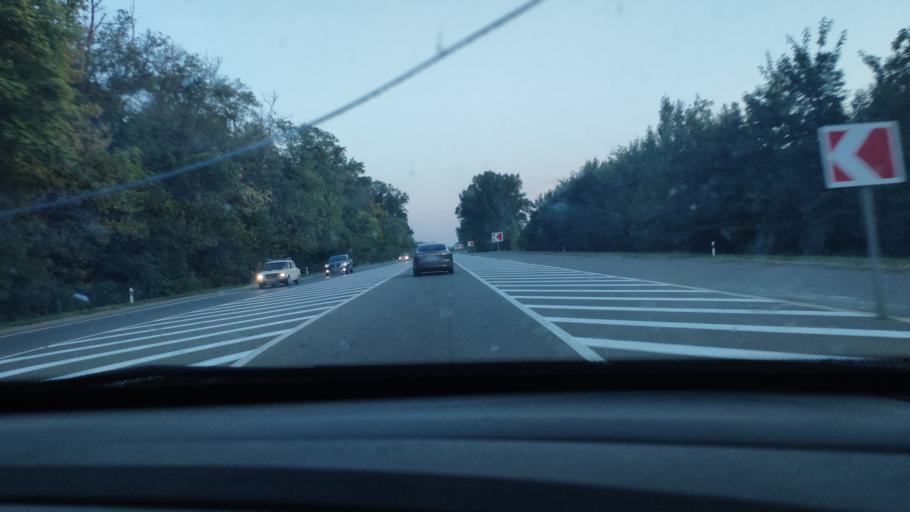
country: RU
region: Krasnodarskiy
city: Medvedovskaya
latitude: 45.4611
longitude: 38.9854
